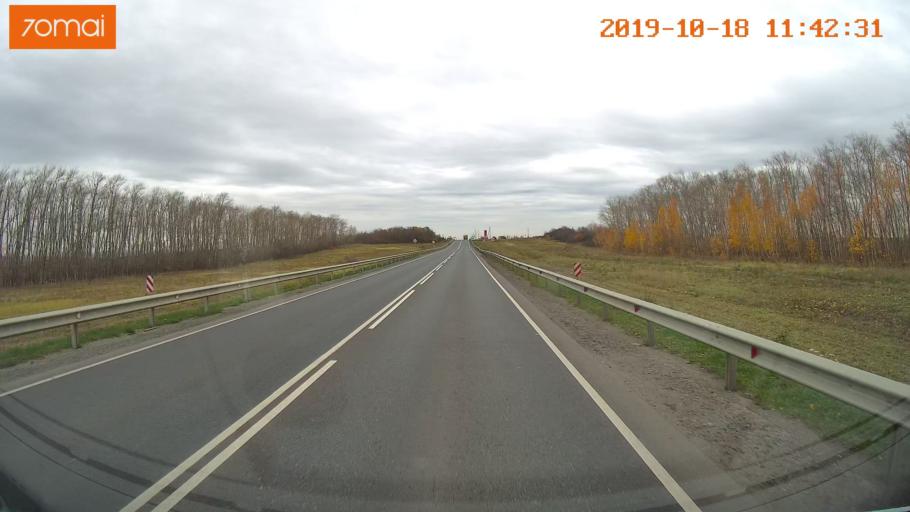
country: RU
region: Rjazan
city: Oktyabr'skiy
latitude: 54.1891
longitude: 38.9293
